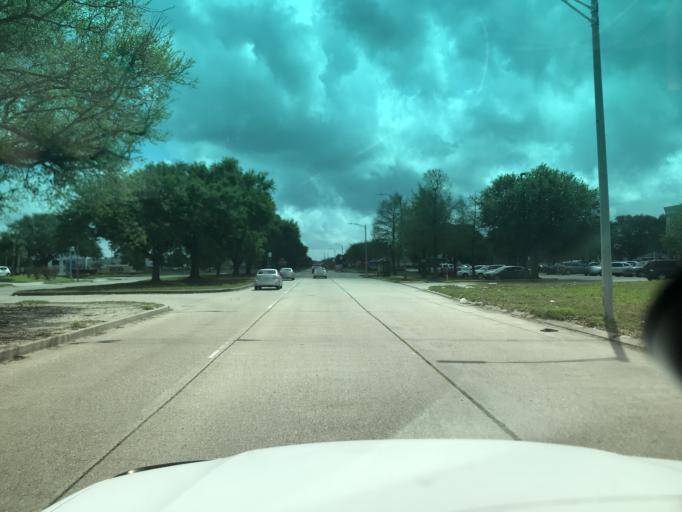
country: US
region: Louisiana
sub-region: Saint Bernard Parish
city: Chalmette
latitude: 30.0397
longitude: -89.9559
